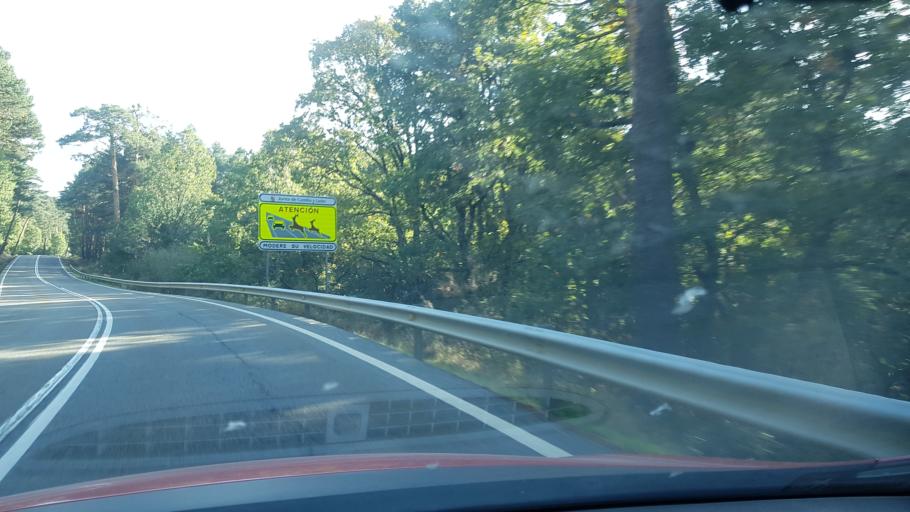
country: ES
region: Castille and Leon
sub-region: Provincia de Segovia
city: San Ildefonso
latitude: 40.8498
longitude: -4.0263
